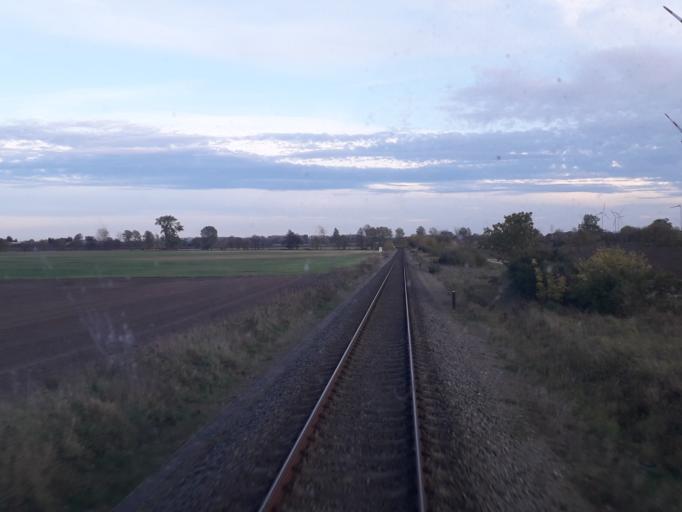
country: DE
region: Brandenburg
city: Dabergotz
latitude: 52.9372
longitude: 12.7096
